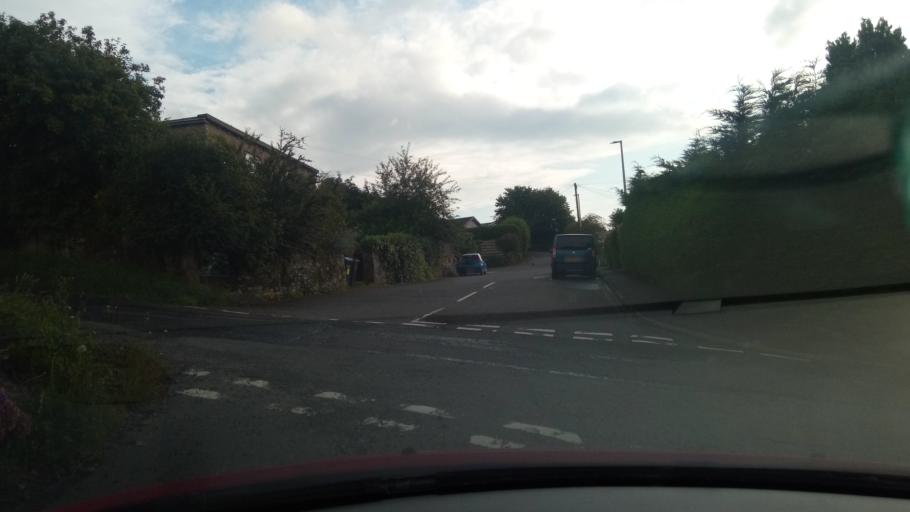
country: GB
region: Scotland
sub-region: The Scottish Borders
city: Hawick
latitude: 55.4197
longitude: -2.7810
